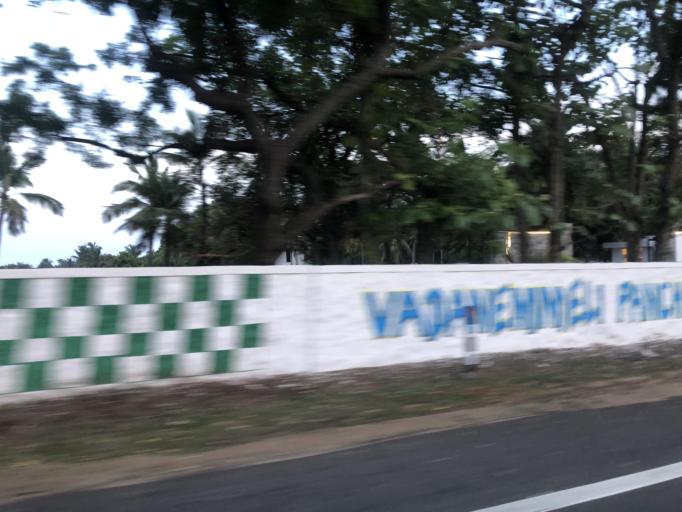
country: IN
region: Tamil Nadu
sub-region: Kancheepuram
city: Mamallapuram
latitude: 12.7467
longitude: 80.2396
